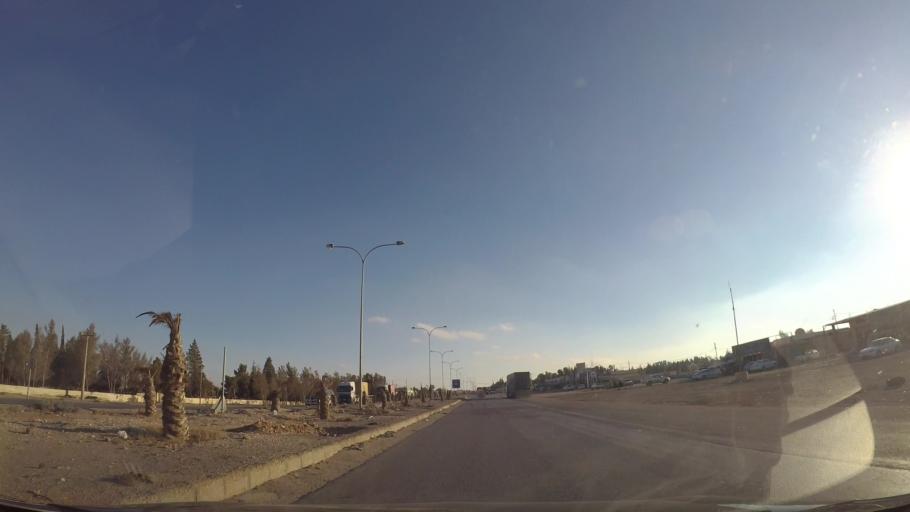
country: JO
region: Tafielah
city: Busayra
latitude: 30.6004
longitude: 35.8049
